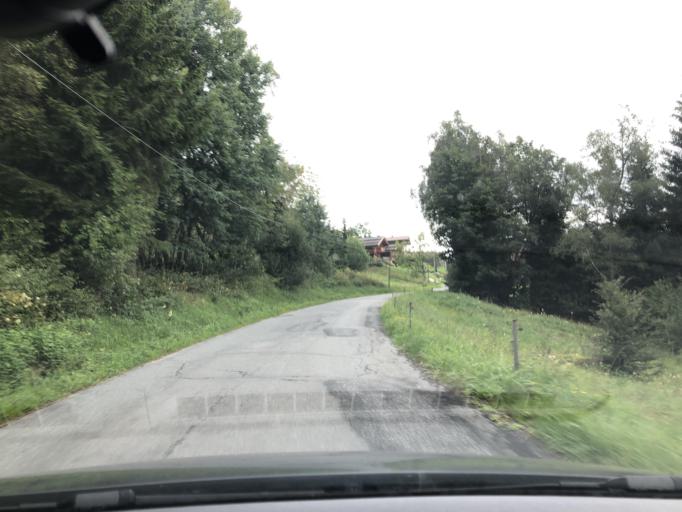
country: FR
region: Rhone-Alpes
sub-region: Departement de la Haute-Savoie
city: Combloux
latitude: 45.8962
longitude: 6.6191
